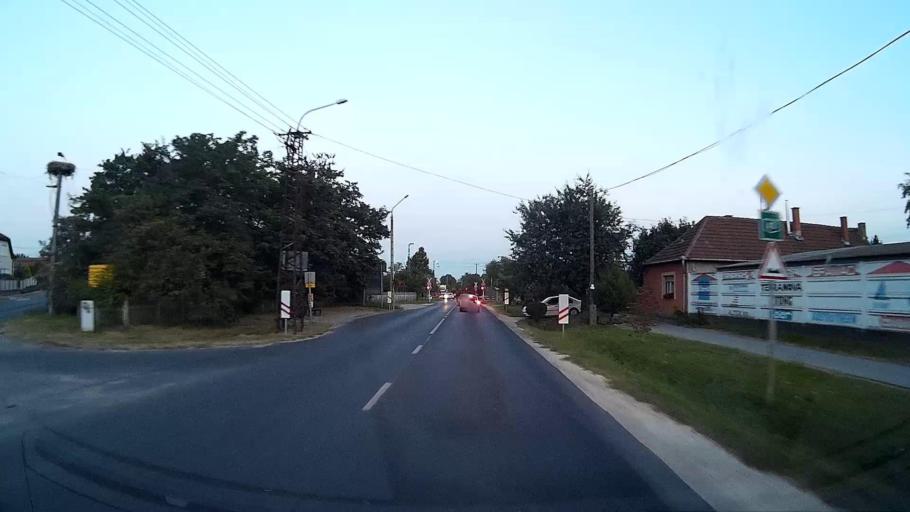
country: HU
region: Pest
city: Cegledbercel
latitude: 47.2121
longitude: 19.6801
